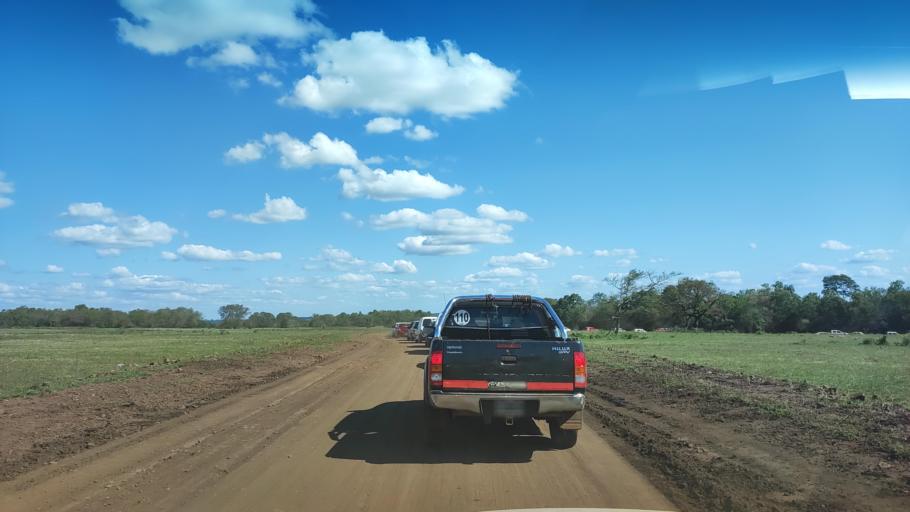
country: PY
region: Itapua
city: Carmen del Parana
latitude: -27.4159
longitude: -56.1718
